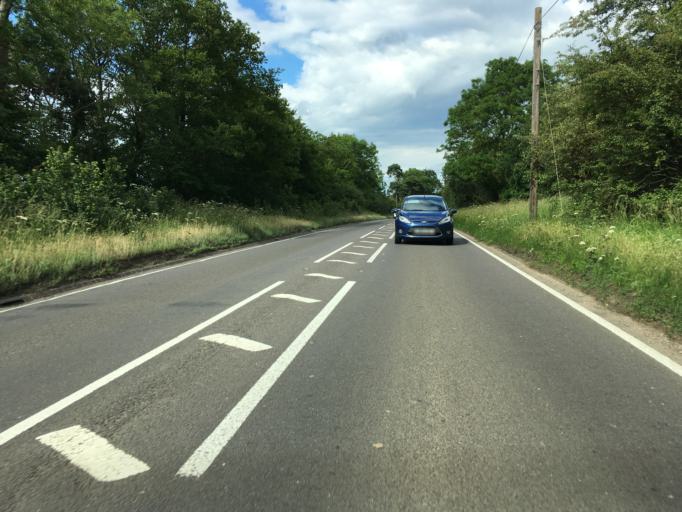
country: GB
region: England
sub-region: Buckinghamshire
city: Stewkley
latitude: 51.8750
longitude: -0.7507
